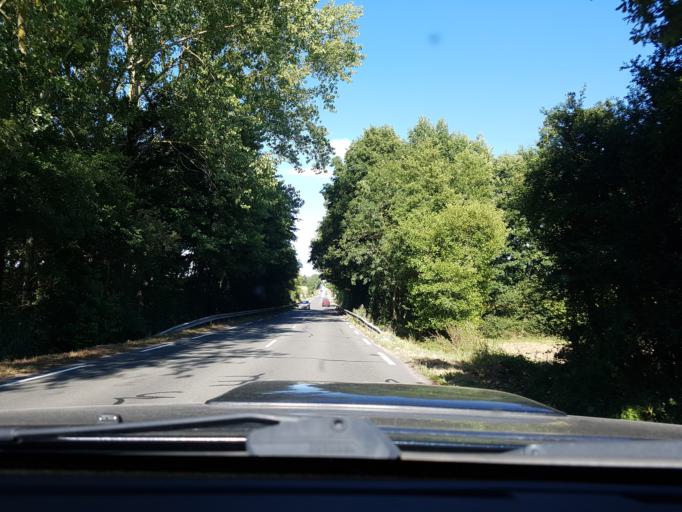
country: FR
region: Pays de la Loire
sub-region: Departement de la Vendee
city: Aizenay
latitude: 46.7304
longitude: -1.6333
